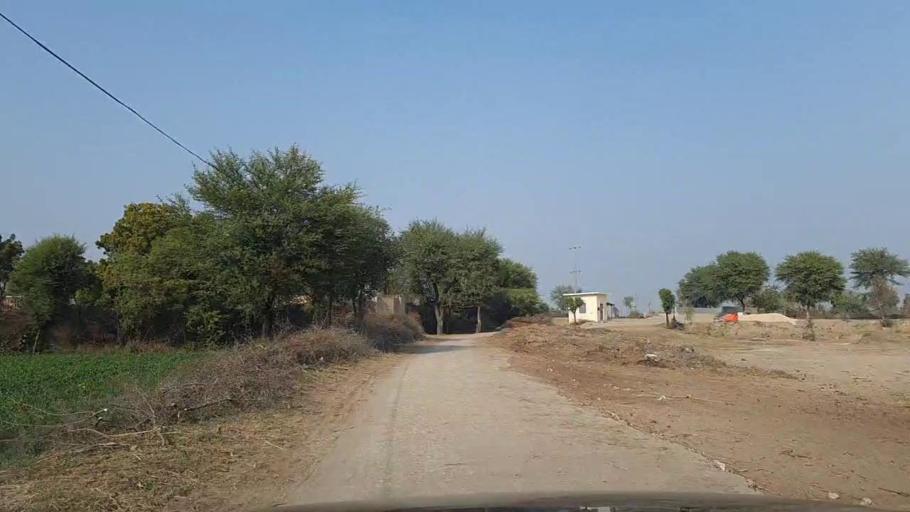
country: PK
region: Sindh
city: Daur
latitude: 26.4305
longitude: 68.4091
